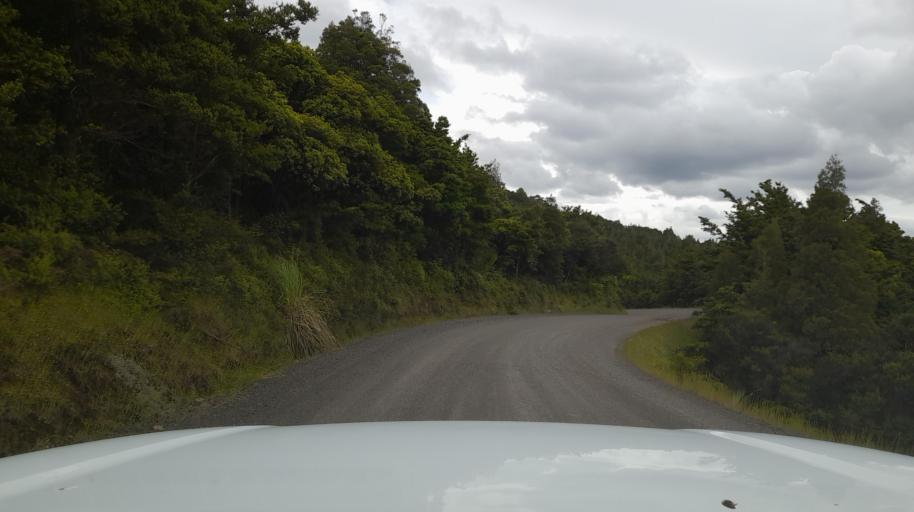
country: NZ
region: Northland
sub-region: Far North District
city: Kaitaia
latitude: -35.3177
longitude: 173.3458
